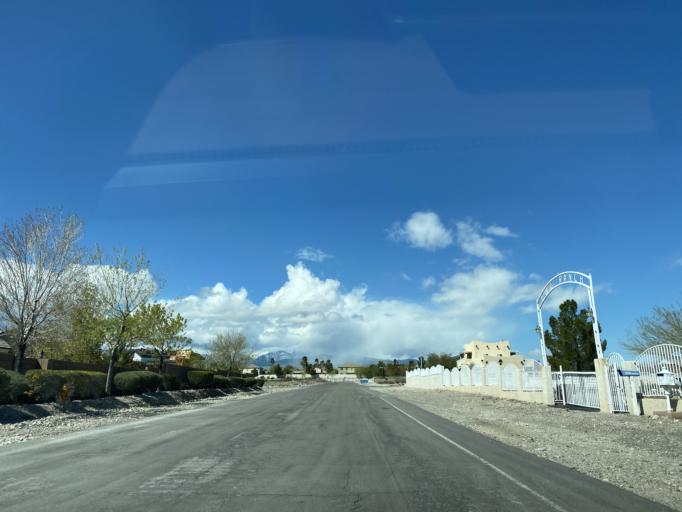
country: US
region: Nevada
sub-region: Clark County
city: North Las Vegas
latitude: 36.3195
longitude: -115.2843
